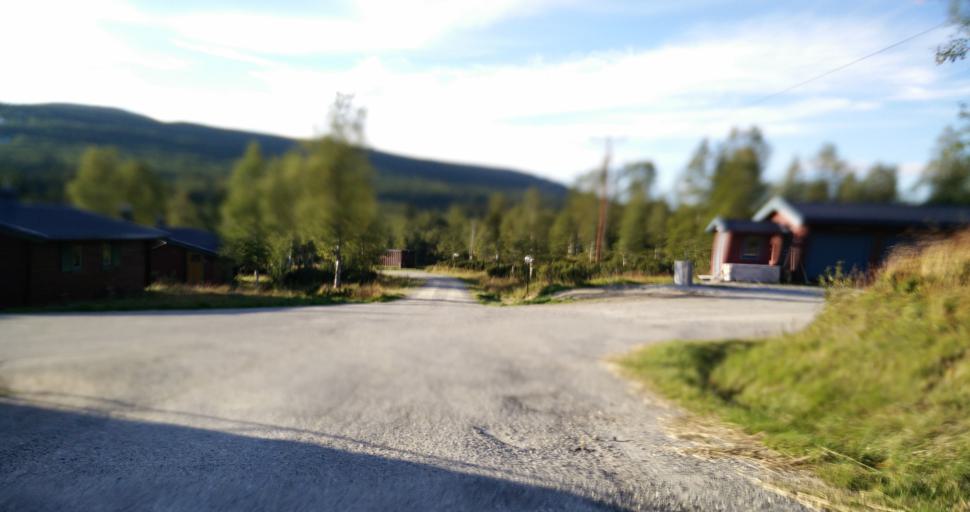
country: NO
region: Sor-Trondelag
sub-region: Tydal
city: Aas
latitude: 62.6433
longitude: 12.4243
